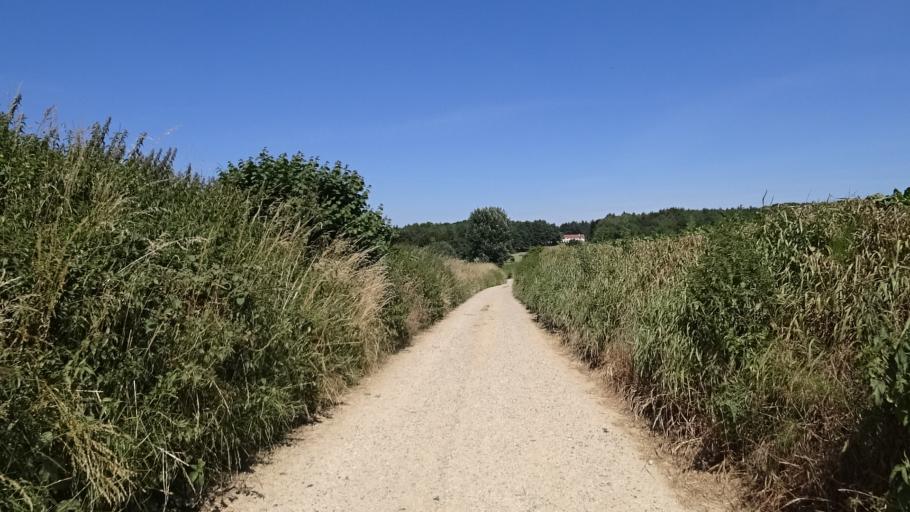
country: BE
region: Wallonia
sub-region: Province du Brabant Wallon
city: Jodoigne
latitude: 50.7074
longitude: 4.8647
